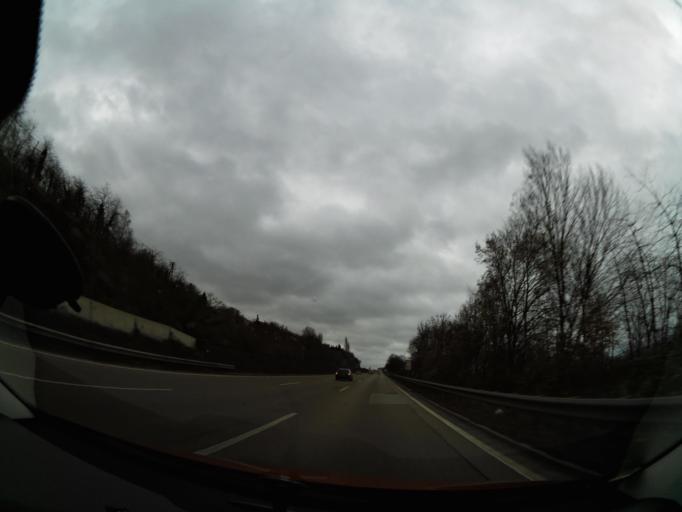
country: DE
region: Rheinland-Pfalz
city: Weitersburg
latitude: 50.4128
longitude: 7.5885
